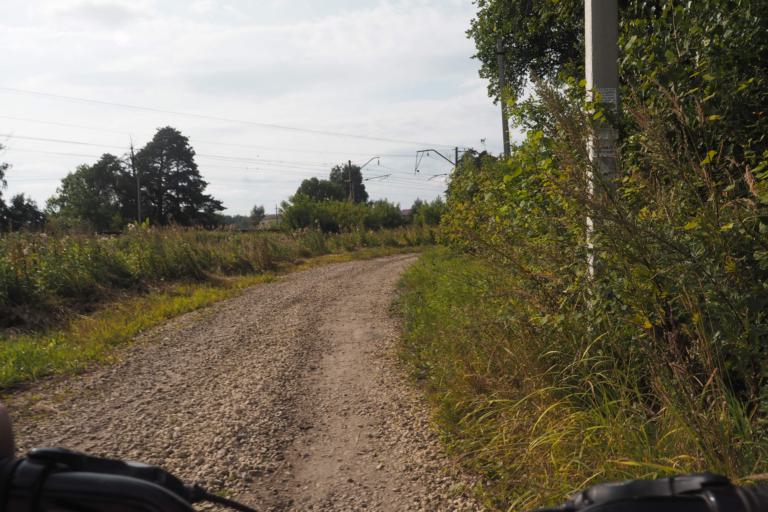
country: RU
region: Moskovskaya
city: Malyshevo
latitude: 55.5345
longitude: 38.3085
